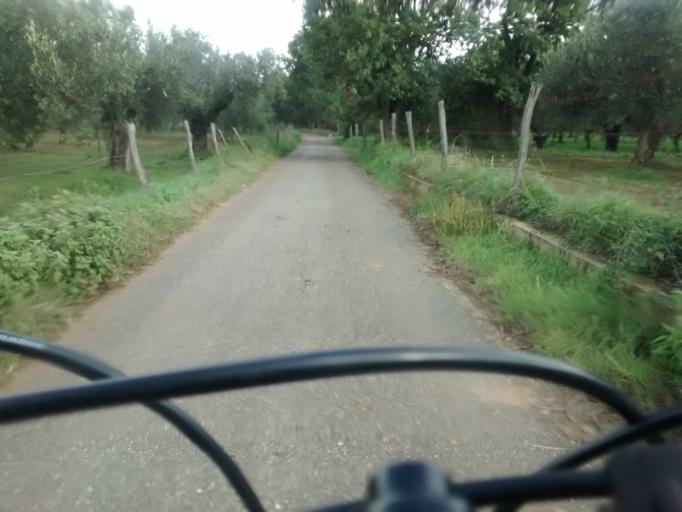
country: IT
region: Calabria
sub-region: Provincia di Catanzaro
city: Maida
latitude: 38.8808
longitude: 16.3901
